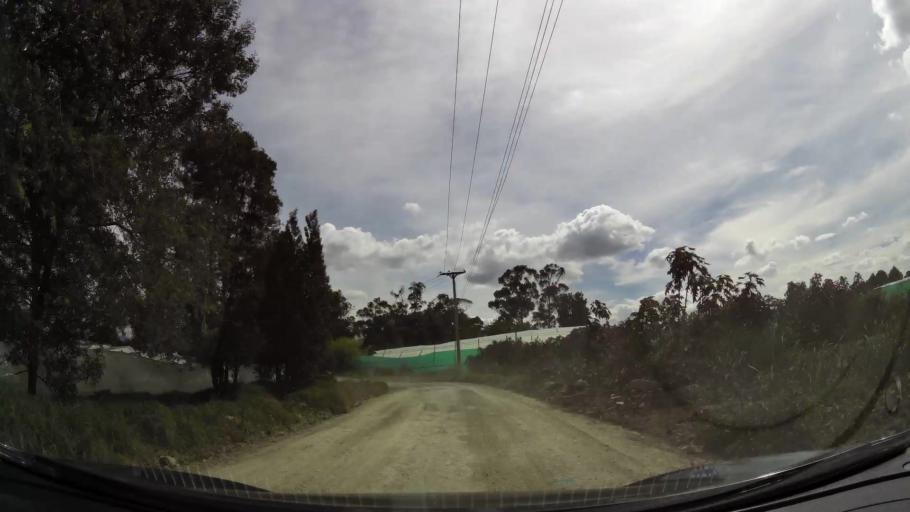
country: CO
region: Cundinamarca
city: Funza
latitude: 4.7041
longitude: -74.1807
